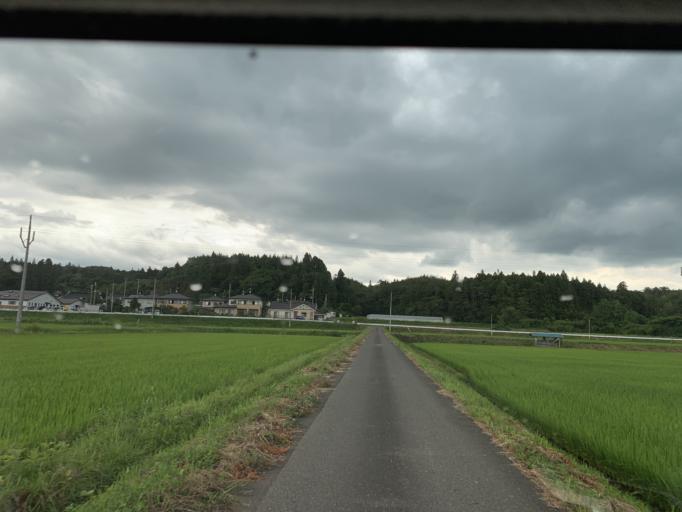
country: JP
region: Iwate
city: Ichinoseki
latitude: 38.9478
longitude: 141.0535
